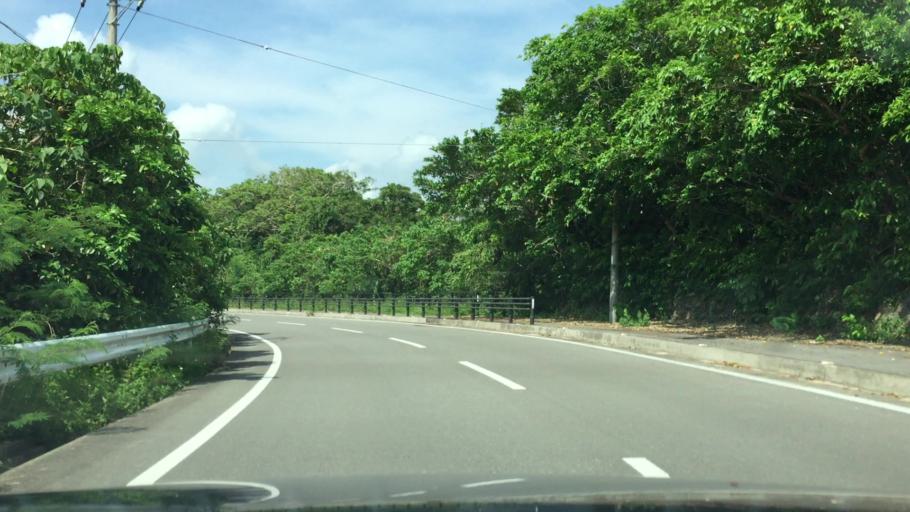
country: JP
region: Okinawa
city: Ishigaki
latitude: 24.4873
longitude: 124.2314
